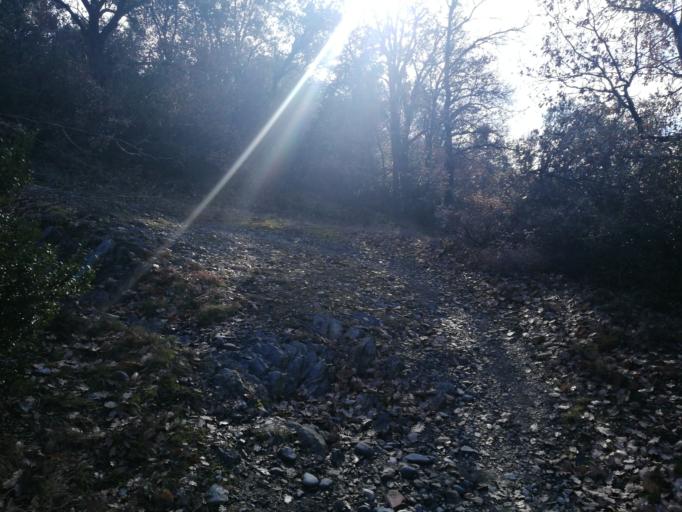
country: ES
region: Catalonia
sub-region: Provincia de Lleida
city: la Seu d'Urgell
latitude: 42.3483
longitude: 1.4385
